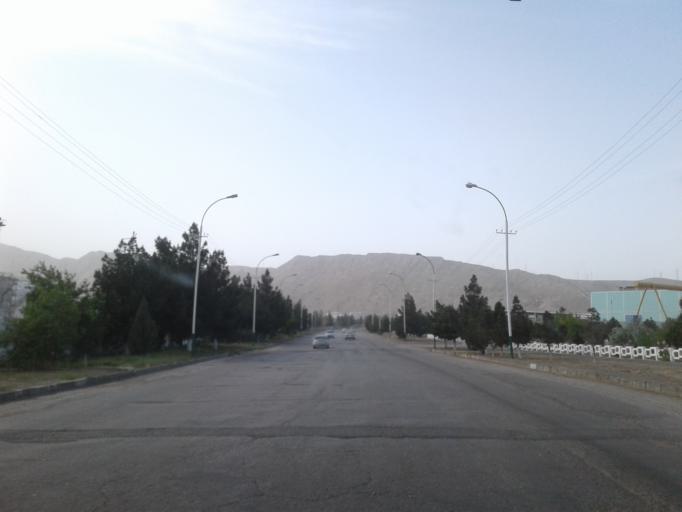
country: TM
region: Balkan
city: Turkmenbasy
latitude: 40.0265
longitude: 52.9679
